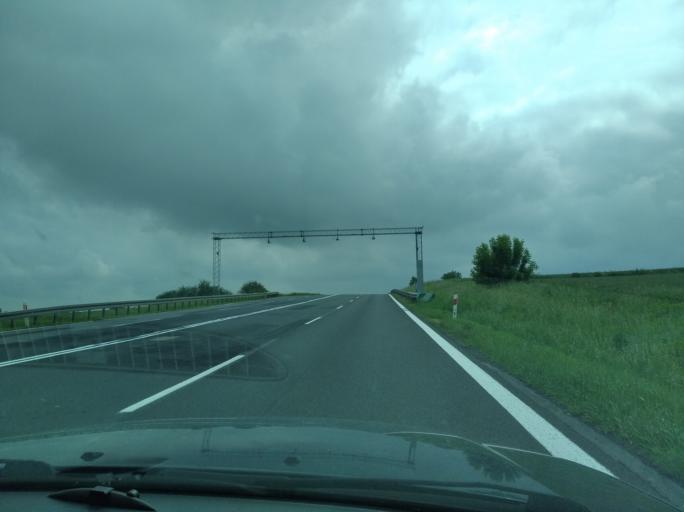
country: PL
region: Subcarpathian Voivodeship
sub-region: Powiat przeworski
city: Rozborz
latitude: 50.0491
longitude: 22.5316
